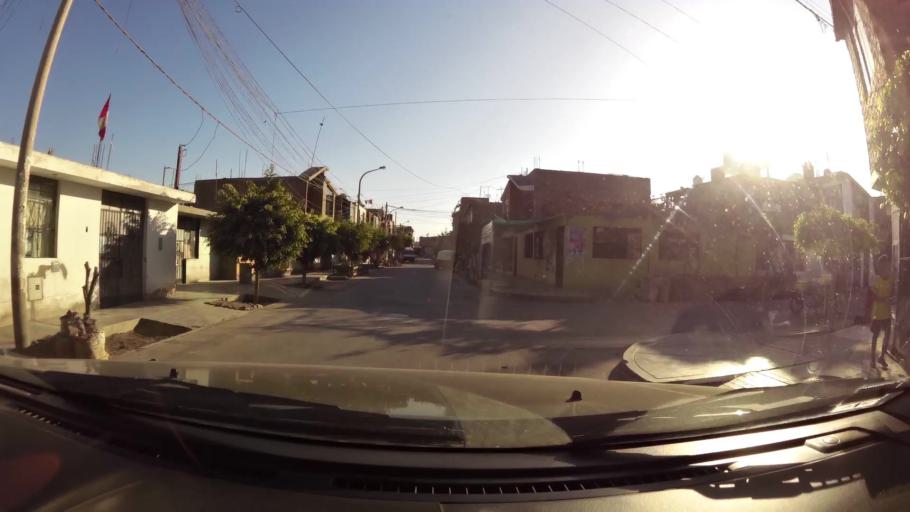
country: PE
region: Ica
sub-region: Provincia de Ica
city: Ica
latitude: -14.0710
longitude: -75.7168
